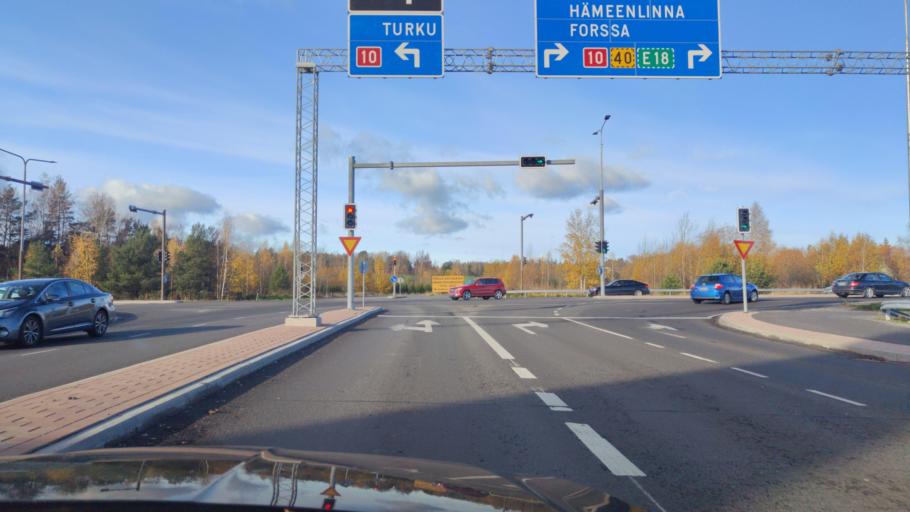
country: FI
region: Varsinais-Suomi
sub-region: Turku
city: Kaarina
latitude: 60.4666
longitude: 22.3479
